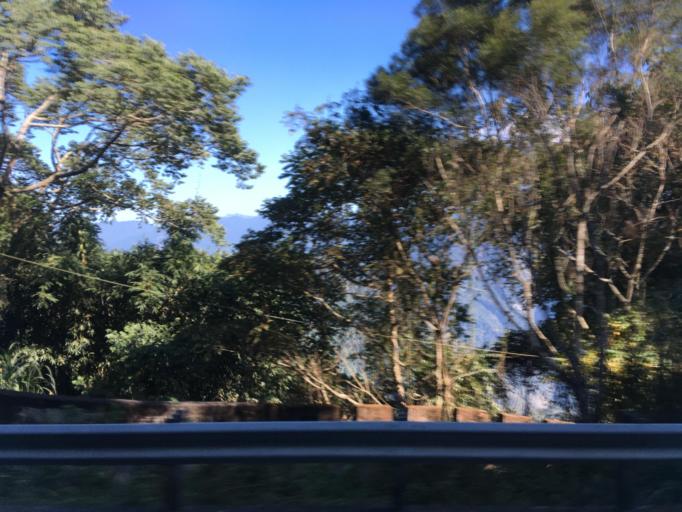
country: TW
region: Taiwan
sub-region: Chiayi
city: Jiayi Shi
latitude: 23.4348
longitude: 120.6632
